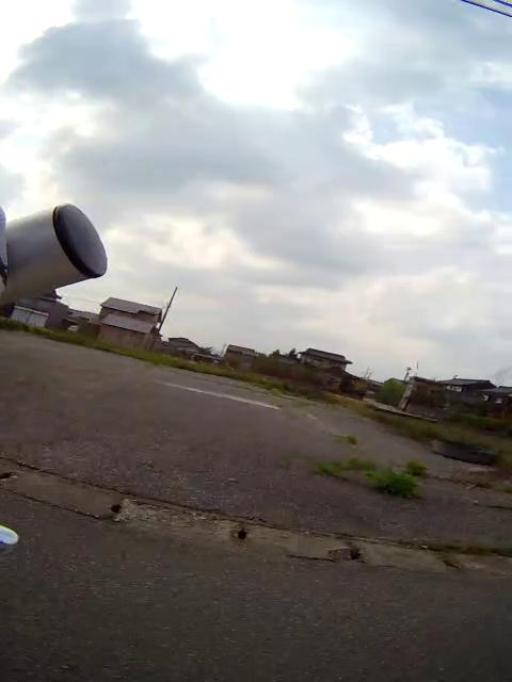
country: JP
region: Toyama
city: Takaoka
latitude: 36.7087
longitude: 136.9882
